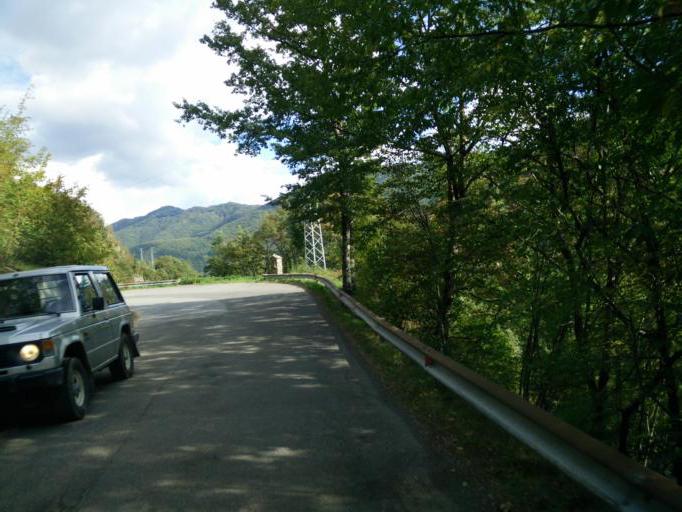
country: IT
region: Tuscany
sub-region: Provincia di Massa-Carrara
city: Zeri
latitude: 44.3493
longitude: 9.7795
